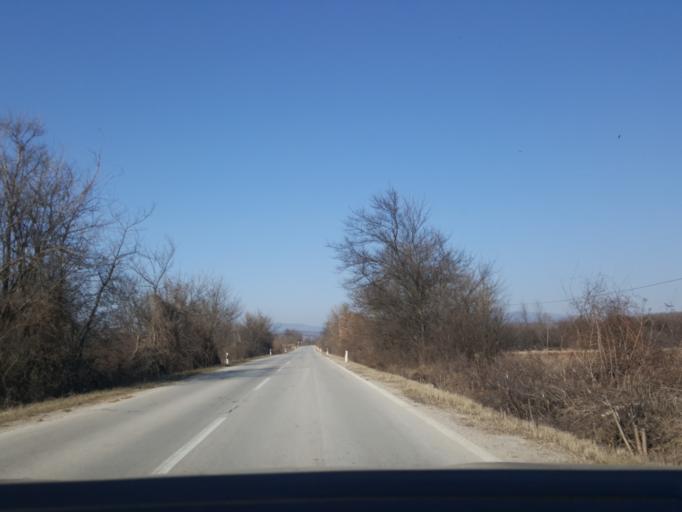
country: RS
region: Central Serbia
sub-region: Nisavski Okrug
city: Nis
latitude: 43.4152
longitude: 21.7973
